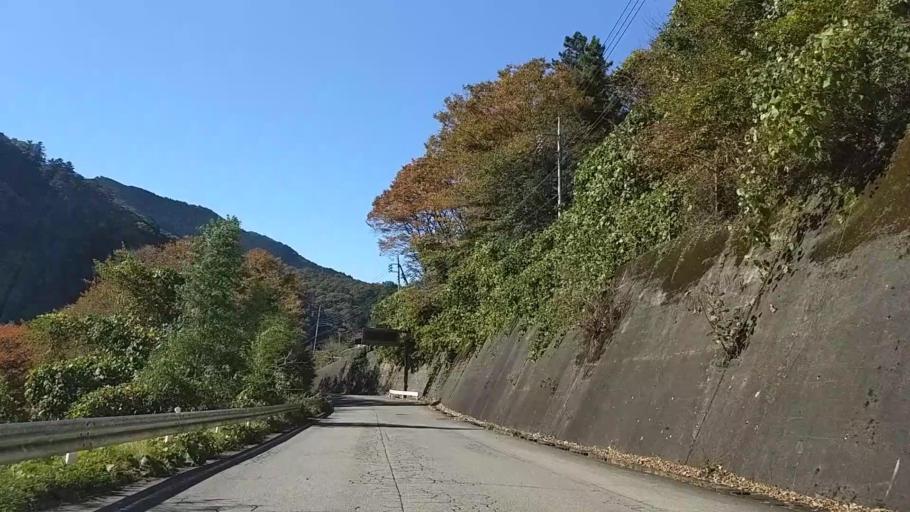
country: JP
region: Yamanashi
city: Uenohara
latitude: 35.6809
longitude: 139.0664
